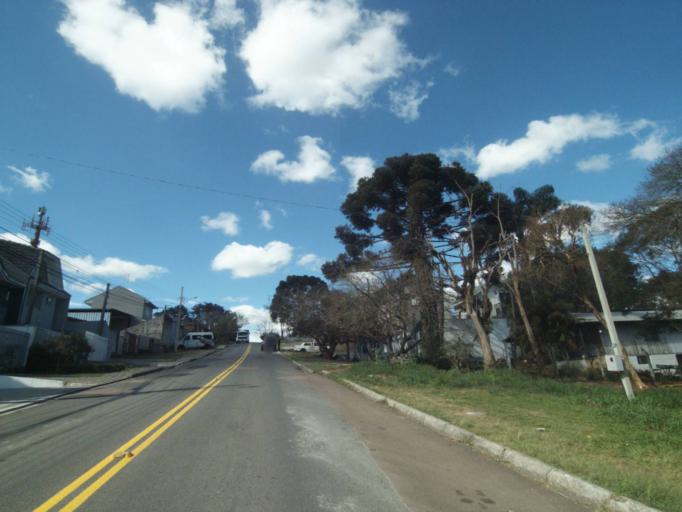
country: BR
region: Parana
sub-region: Curitiba
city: Curitiba
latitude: -25.3859
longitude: -49.2581
